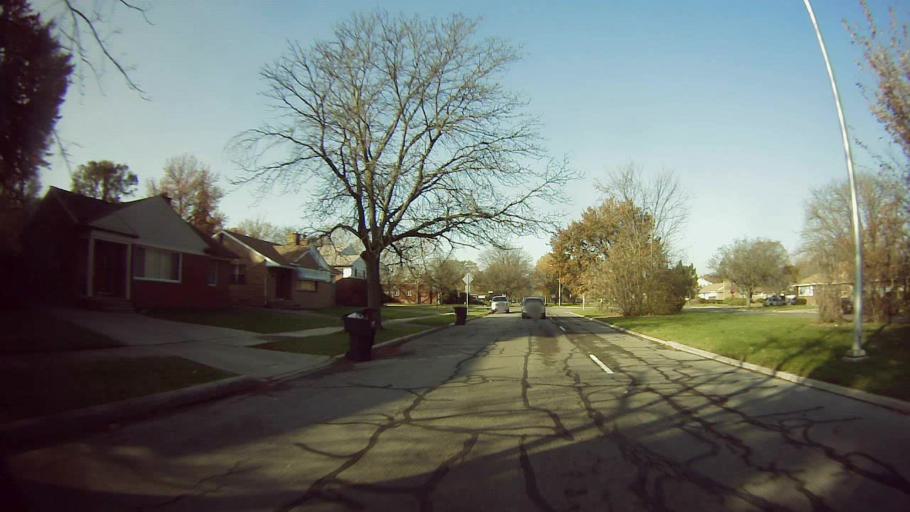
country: US
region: Michigan
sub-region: Wayne County
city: Dearborn
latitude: 42.3564
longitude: -83.1655
